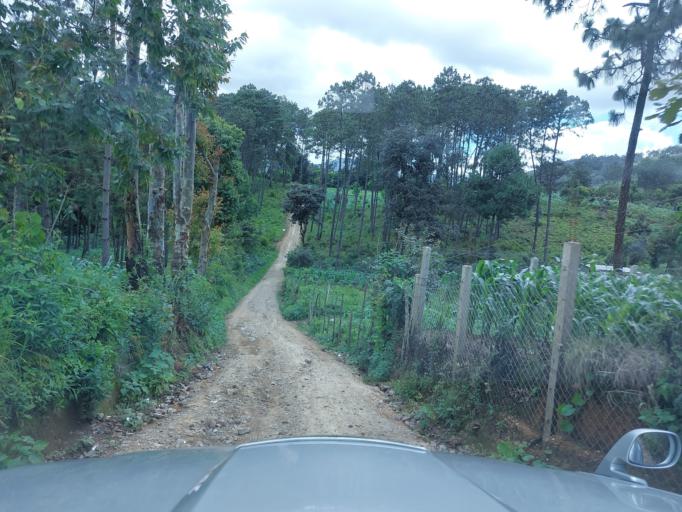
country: GT
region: Chimaltenango
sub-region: Municipio de Chimaltenango
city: Chimaltenango
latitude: 14.6472
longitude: -90.8224
